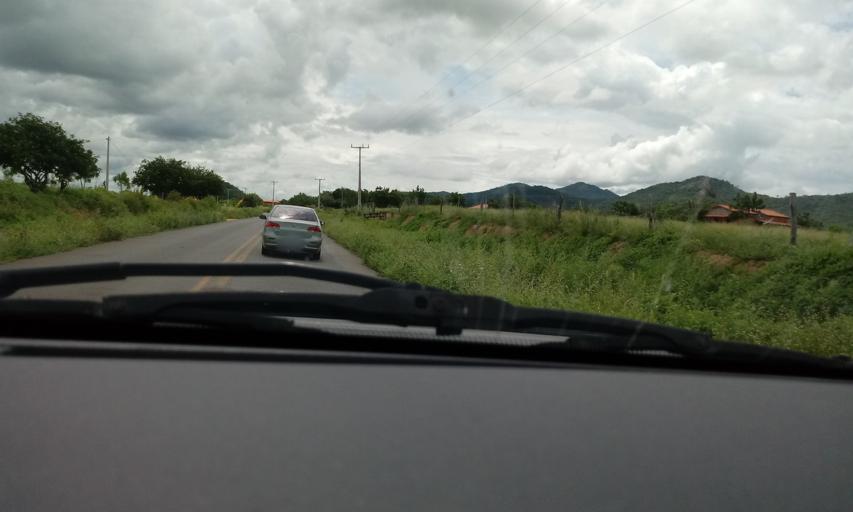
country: BR
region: Bahia
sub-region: Guanambi
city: Guanambi
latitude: -14.1252
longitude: -42.8534
